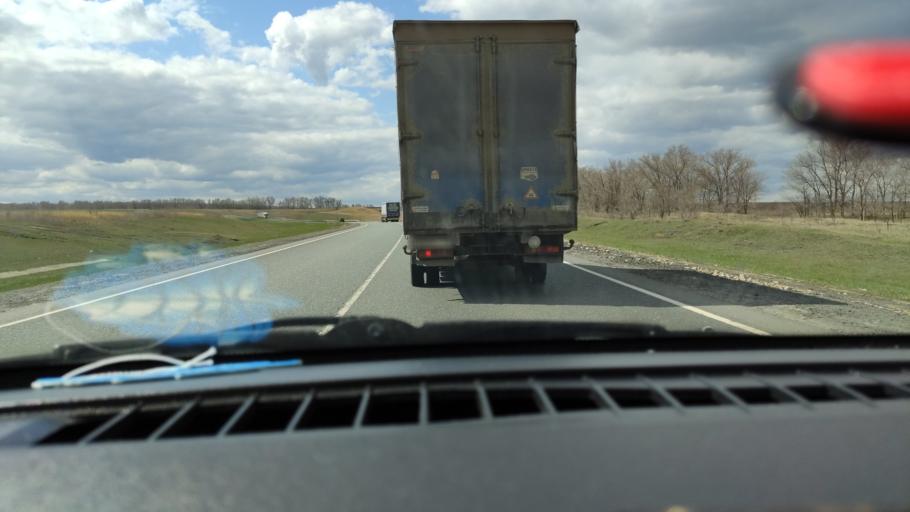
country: RU
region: Saratov
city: Balakovo
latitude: 52.1259
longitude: 47.7548
